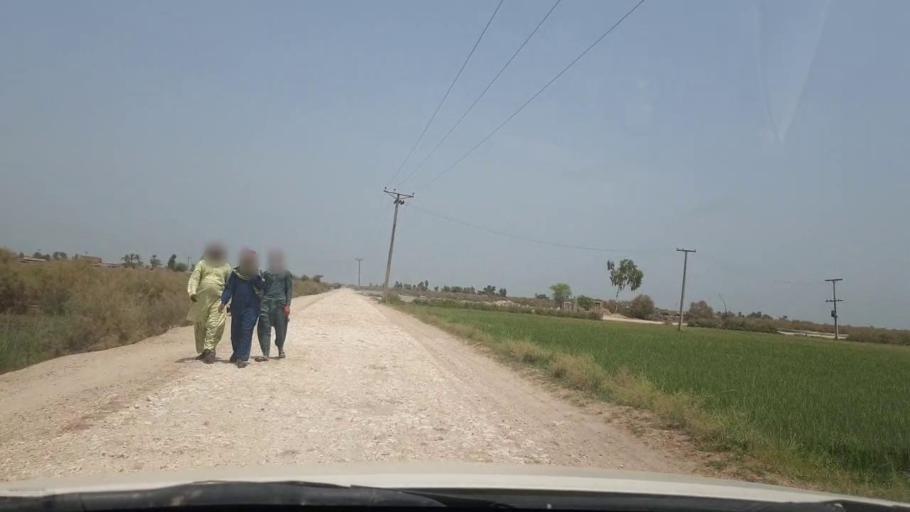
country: PK
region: Sindh
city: Rustam jo Goth
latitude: 28.0530
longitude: 68.8158
